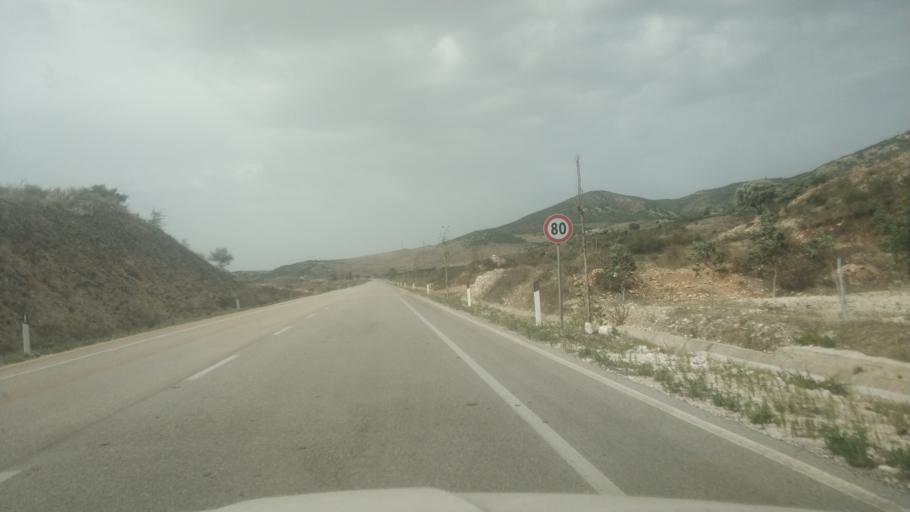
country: AL
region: Gjirokaster
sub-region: Rrethi i Tepelenes
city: Memaliaj
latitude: 40.3576
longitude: 19.9334
